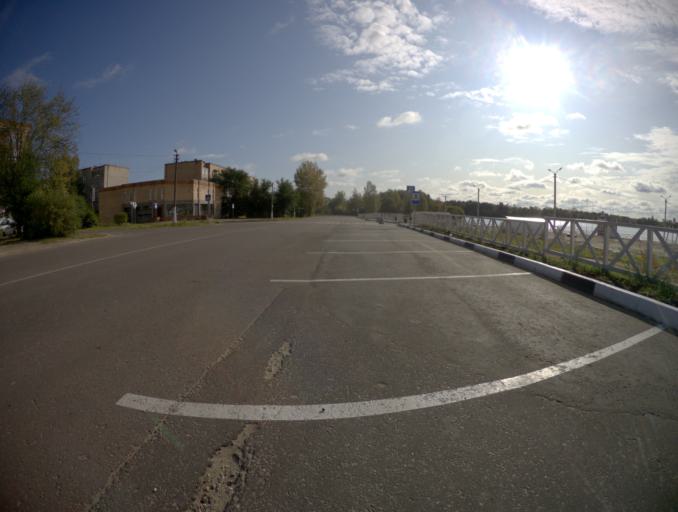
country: RU
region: Moskovskaya
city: Roshal'
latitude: 55.6586
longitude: 39.8524
